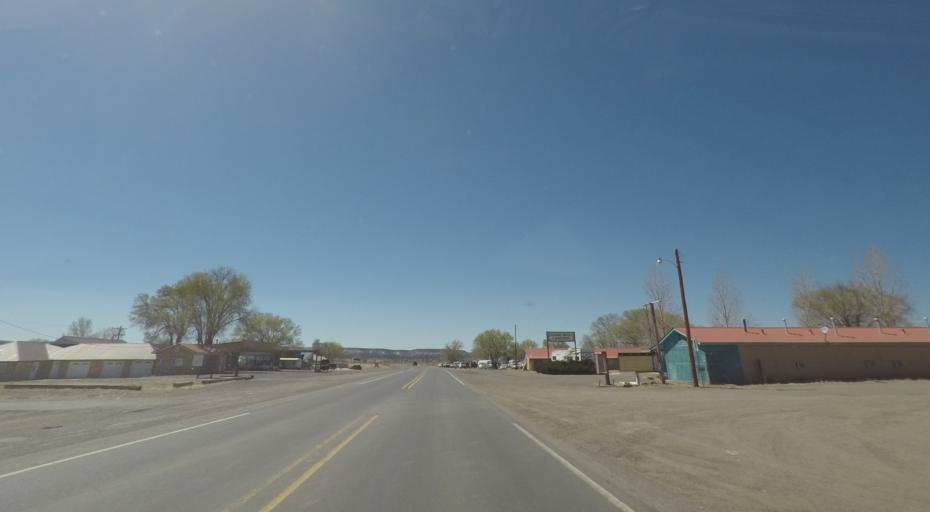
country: US
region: New Mexico
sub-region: Catron County
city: Reserve
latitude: 34.3436
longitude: -108.4981
